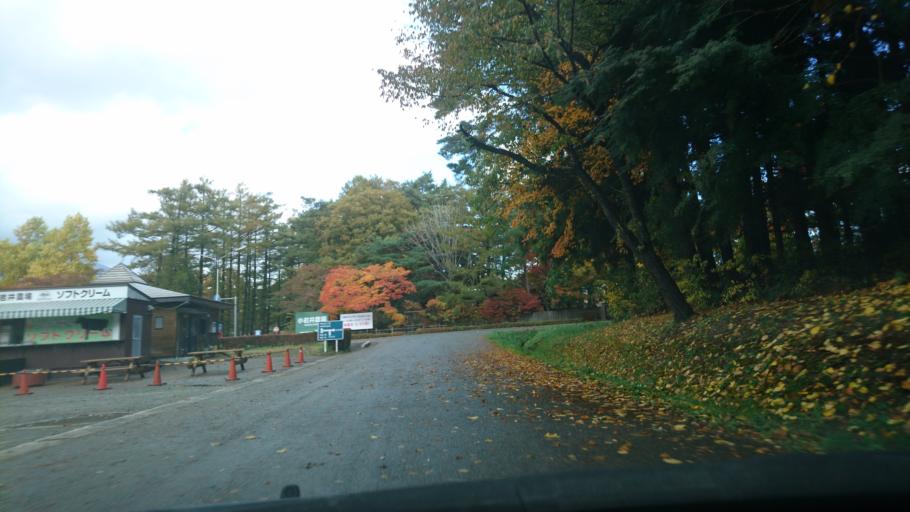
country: JP
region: Iwate
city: Shizukuishi
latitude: 39.7507
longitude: 141.0144
